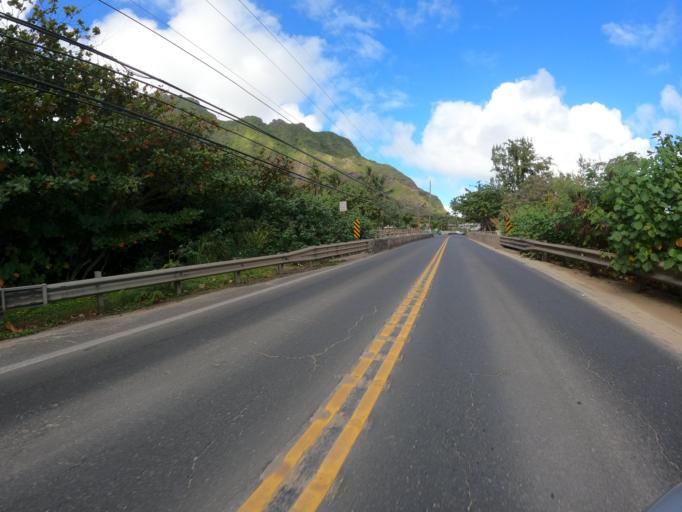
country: US
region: Hawaii
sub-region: Honolulu County
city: Ka'a'awa
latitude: 21.5441
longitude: -157.8458
